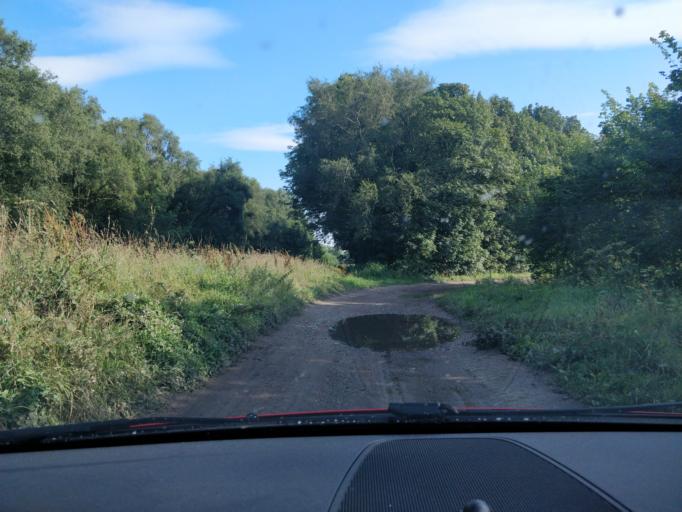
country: GB
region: England
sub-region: Lancashire
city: Banks
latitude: 53.6526
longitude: -2.8996
